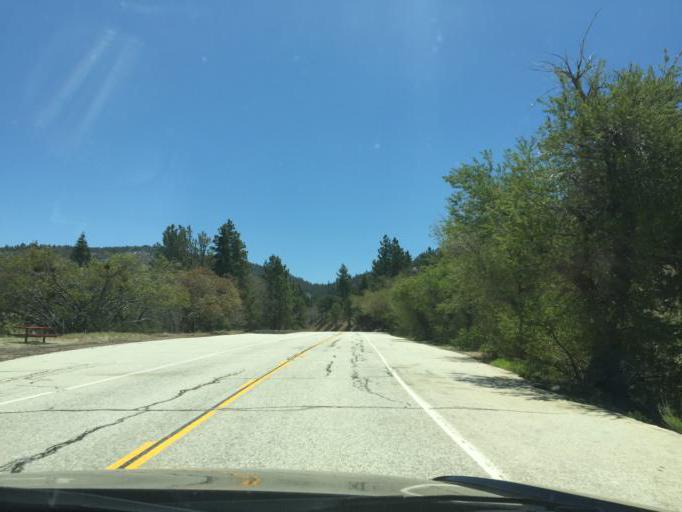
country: US
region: California
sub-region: San Bernardino County
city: Pinon Hills
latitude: 34.3923
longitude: -117.7249
